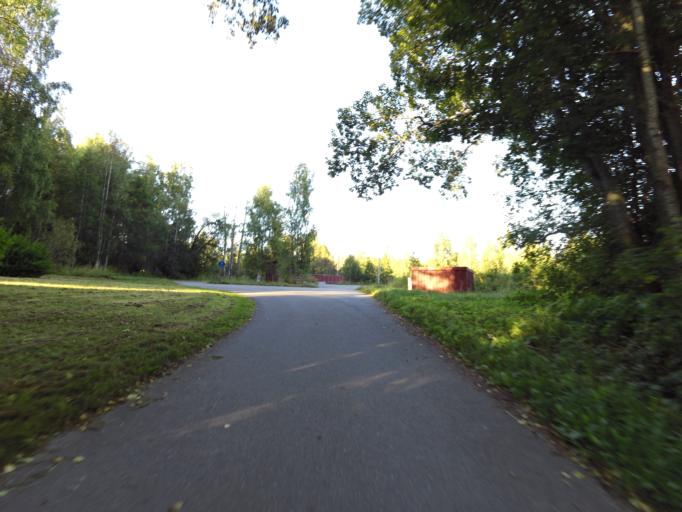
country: SE
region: Gaevleborg
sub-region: Gavle Kommun
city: Gavle
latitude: 60.7174
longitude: 17.1397
